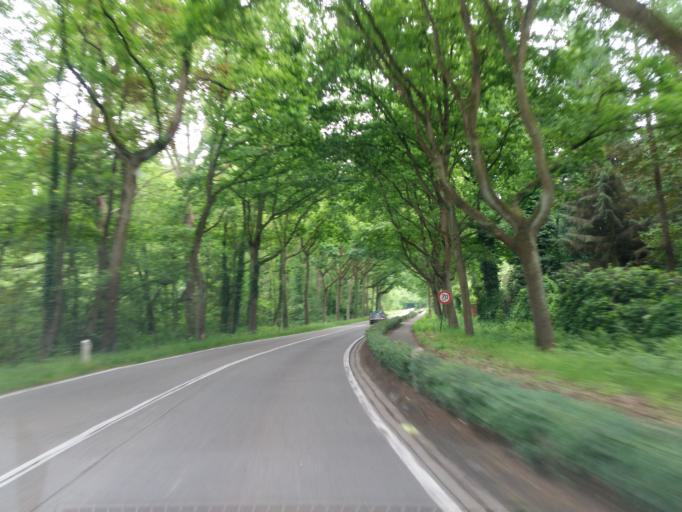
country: BE
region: Flanders
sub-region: Provincie Antwerpen
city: Schilde
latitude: 51.2260
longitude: 4.5984
